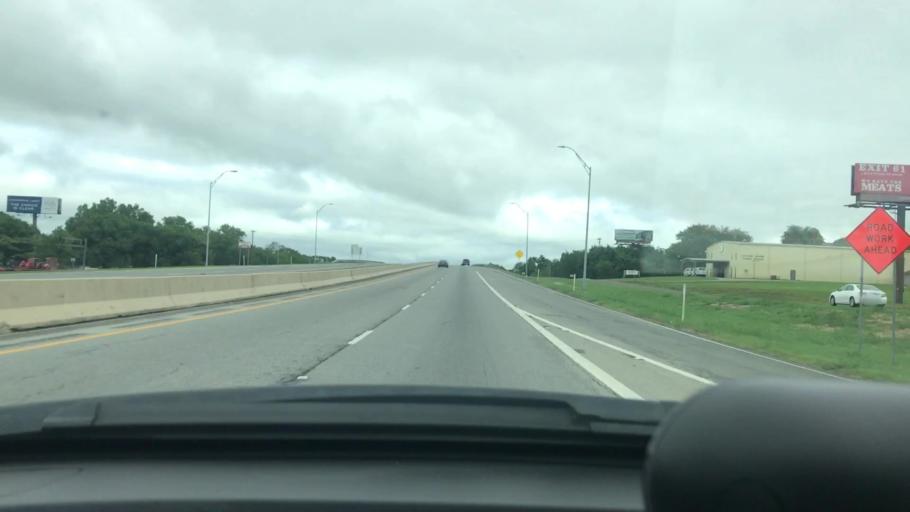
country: US
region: Texas
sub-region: Grayson County
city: Sherman
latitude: 33.6259
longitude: -96.6127
